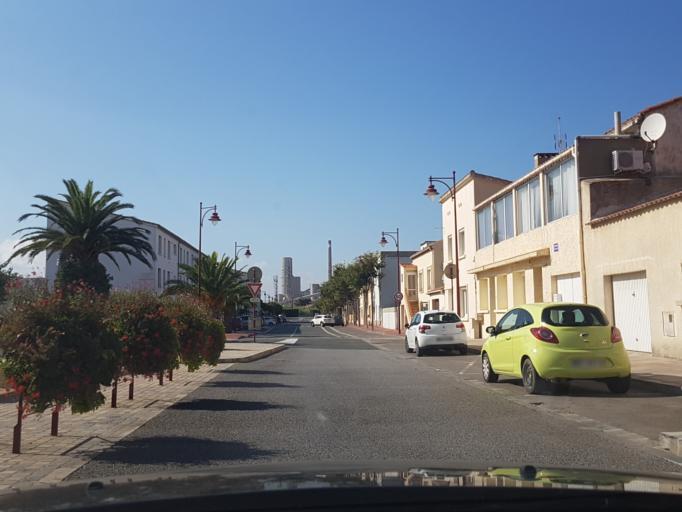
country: FR
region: Languedoc-Roussillon
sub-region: Departement de l'Aude
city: Port-la-Nouvelle
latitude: 43.0205
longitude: 3.0422
